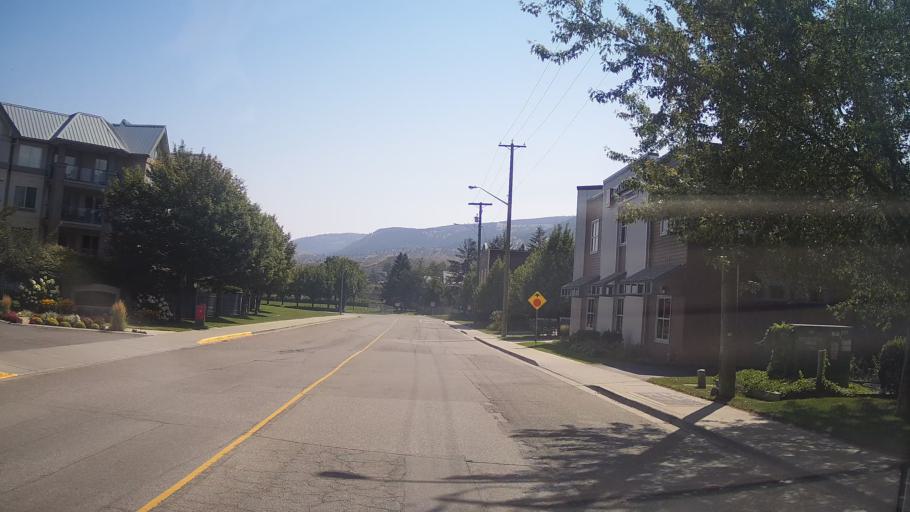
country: CA
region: British Columbia
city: Kamloops
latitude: 50.6760
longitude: -120.3175
